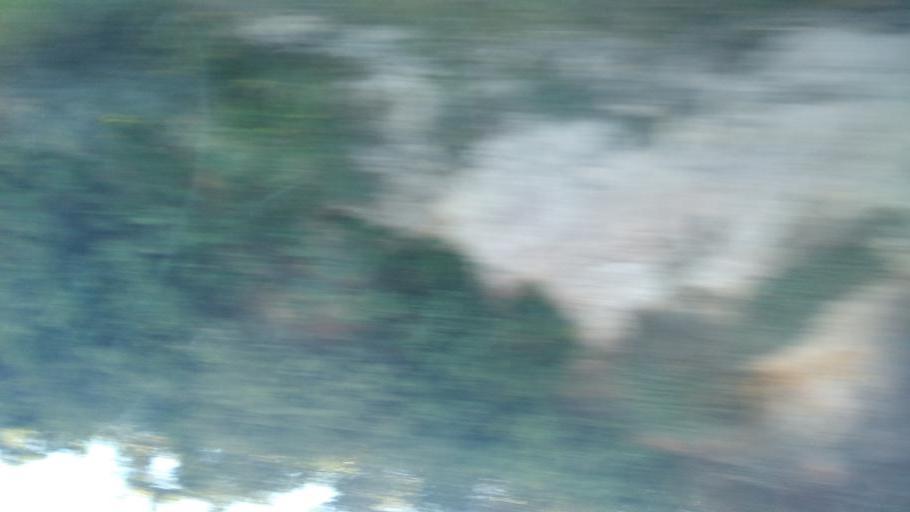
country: ZA
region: Western Cape
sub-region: Overberg District Municipality
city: Caledon
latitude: -34.1295
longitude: 19.2957
